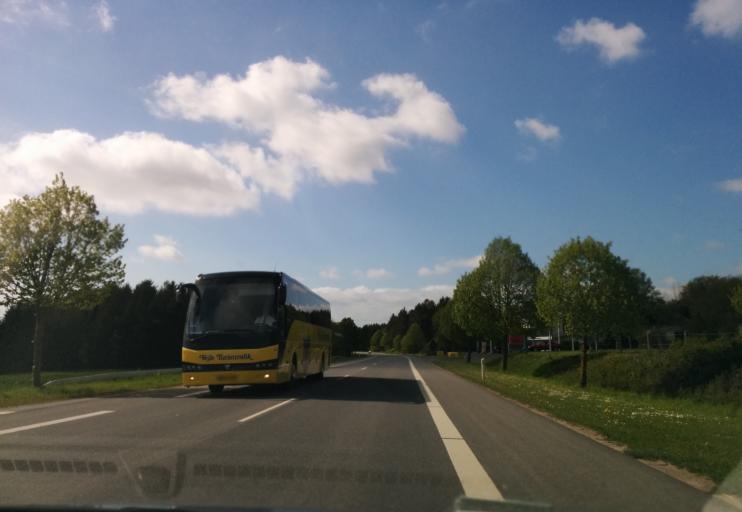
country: DK
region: South Denmark
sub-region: Assens Kommune
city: Arup
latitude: 55.4040
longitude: 10.0845
